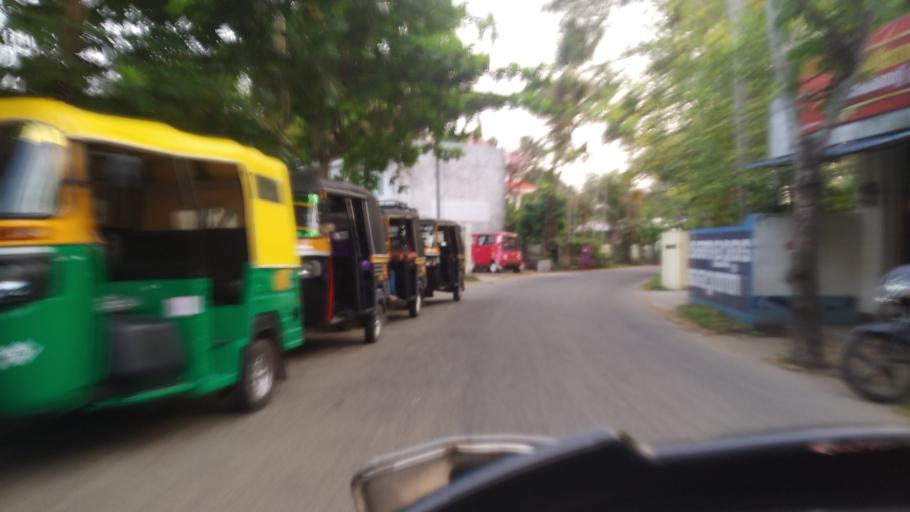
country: IN
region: Kerala
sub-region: Thrissur District
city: Kodungallur
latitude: 10.1807
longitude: 76.2053
